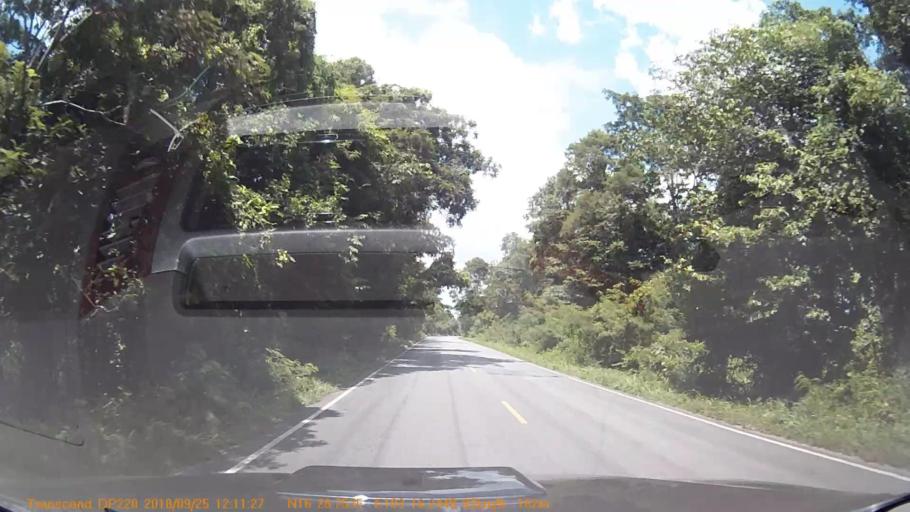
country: TH
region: Kalasin
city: Huai Mek
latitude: 16.4795
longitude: 103.2706
